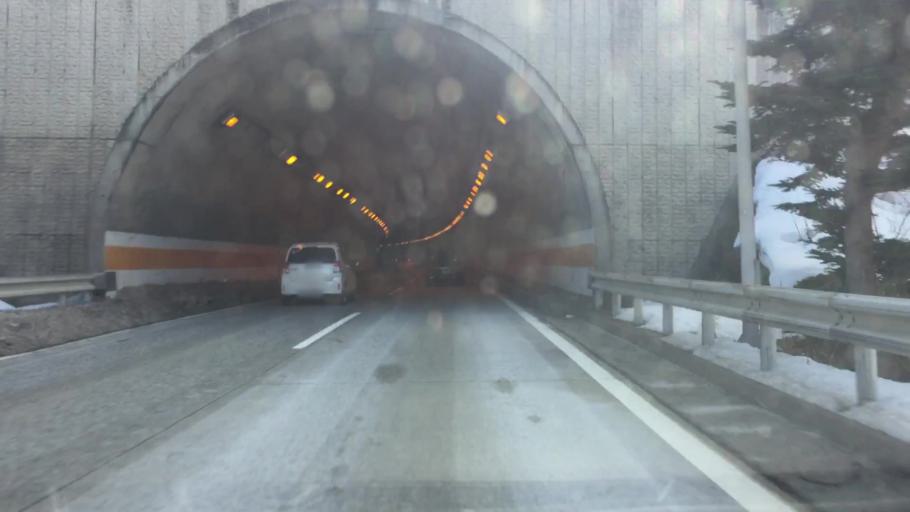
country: JP
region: Gunma
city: Numata
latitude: 36.7268
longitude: 138.9758
